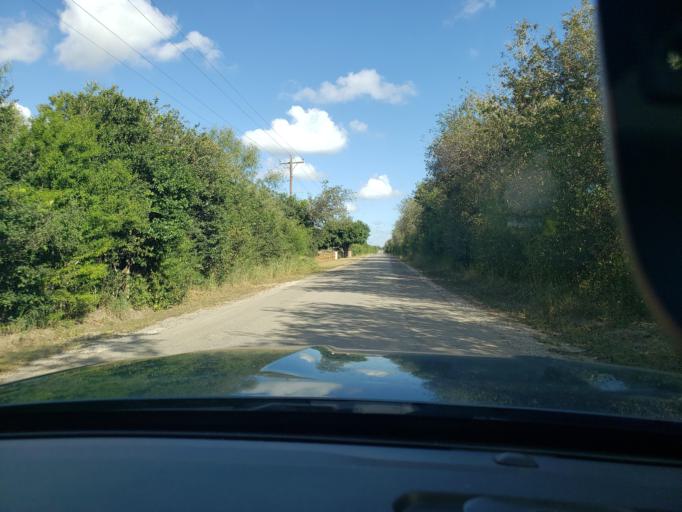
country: US
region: Texas
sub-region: Bee County
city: Beeville
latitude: 28.4510
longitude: -97.7173
